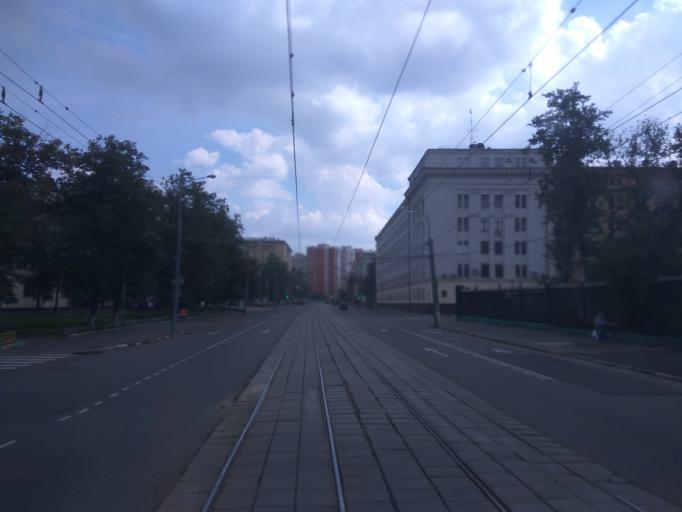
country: RU
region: Moscow
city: Lefortovo
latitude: 55.7551
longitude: 37.7060
